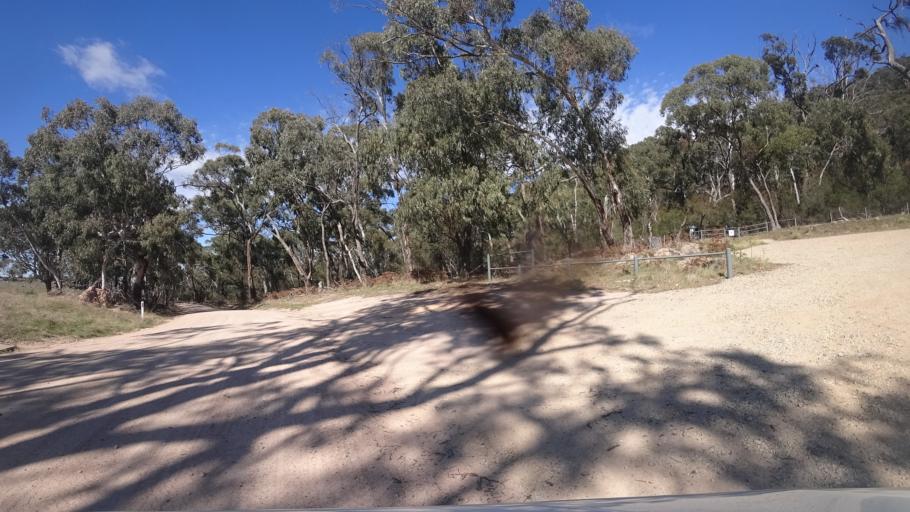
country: AU
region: New South Wales
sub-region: Oberon
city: Oberon
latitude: -33.5376
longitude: 149.9327
